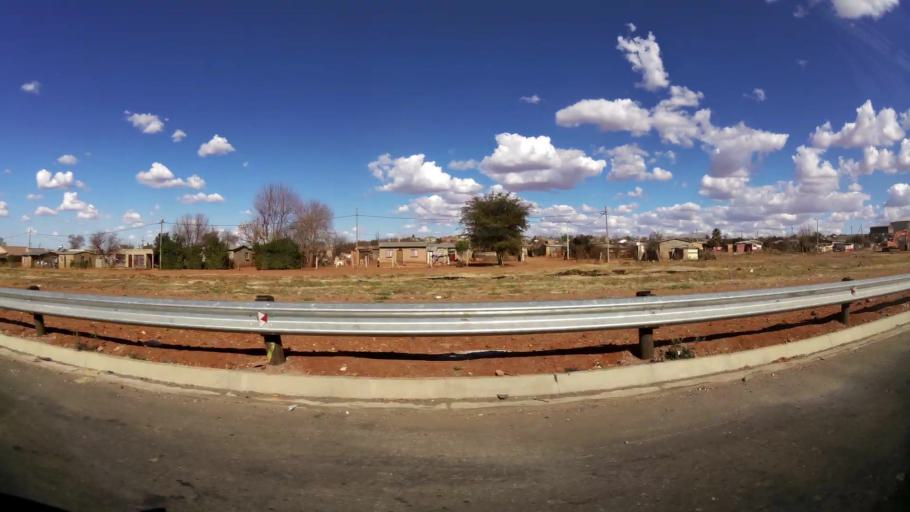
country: ZA
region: North-West
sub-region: Dr Kenneth Kaunda District Municipality
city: Klerksdorp
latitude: -26.8744
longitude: 26.5988
